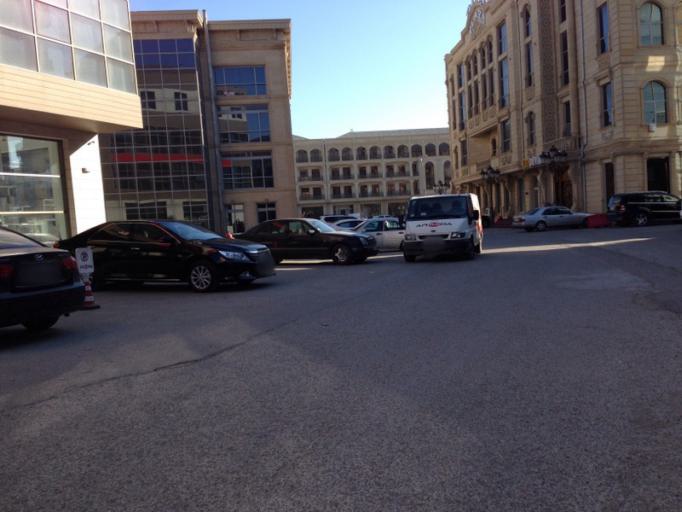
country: AZ
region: Baki
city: Baku
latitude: 40.4082
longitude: 49.8627
